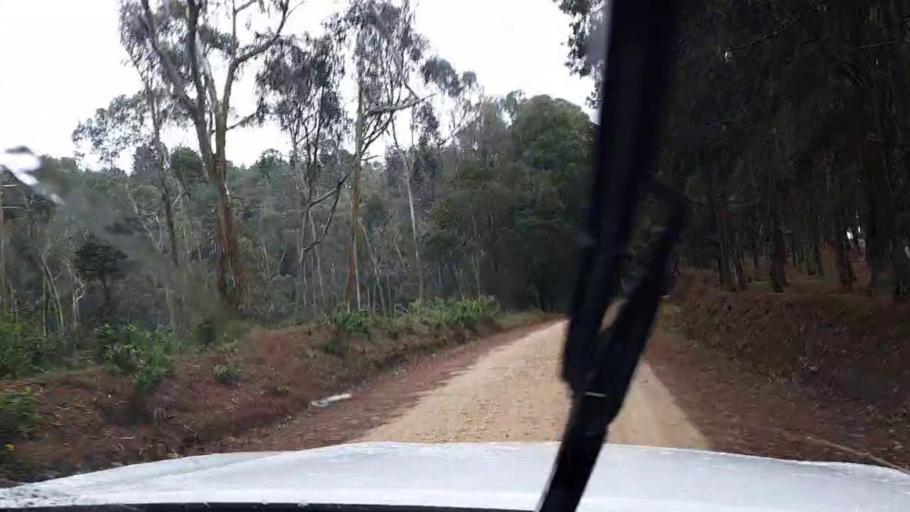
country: RW
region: Southern Province
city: Nzega
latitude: -2.3635
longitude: 29.3804
